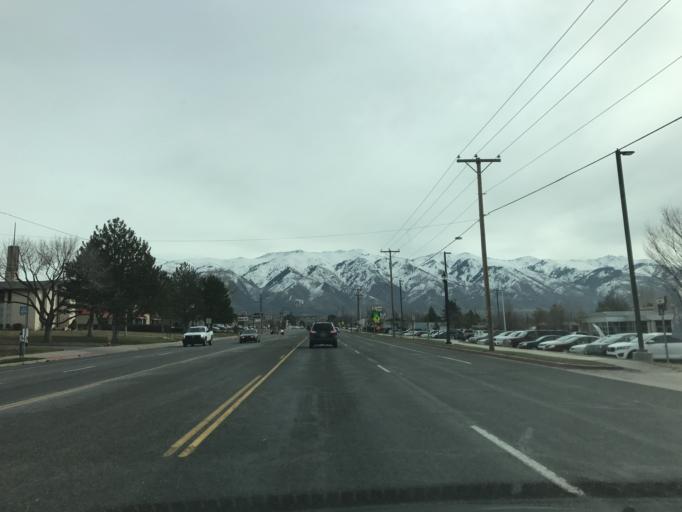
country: US
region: Utah
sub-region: Davis County
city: Hill Air Force Bace
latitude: 41.0892
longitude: -111.9777
